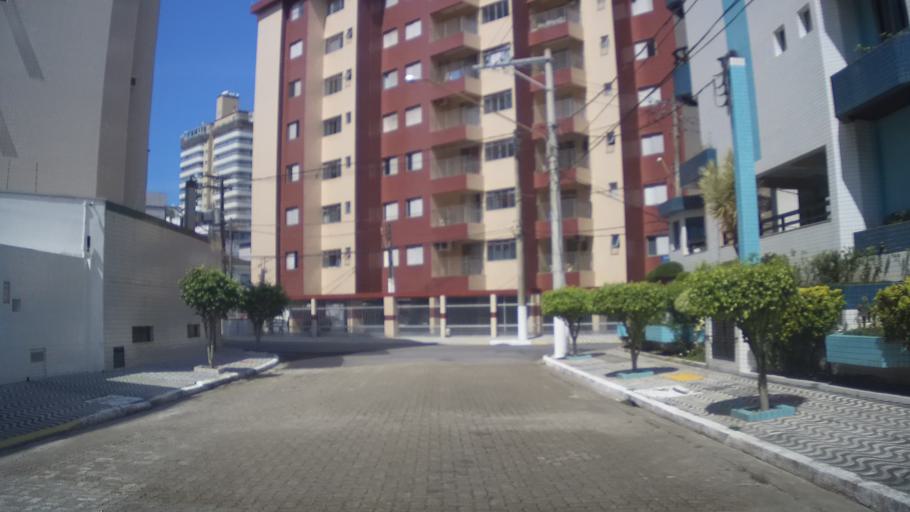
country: BR
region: Sao Paulo
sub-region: Praia Grande
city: Praia Grande
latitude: -24.0112
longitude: -46.4236
